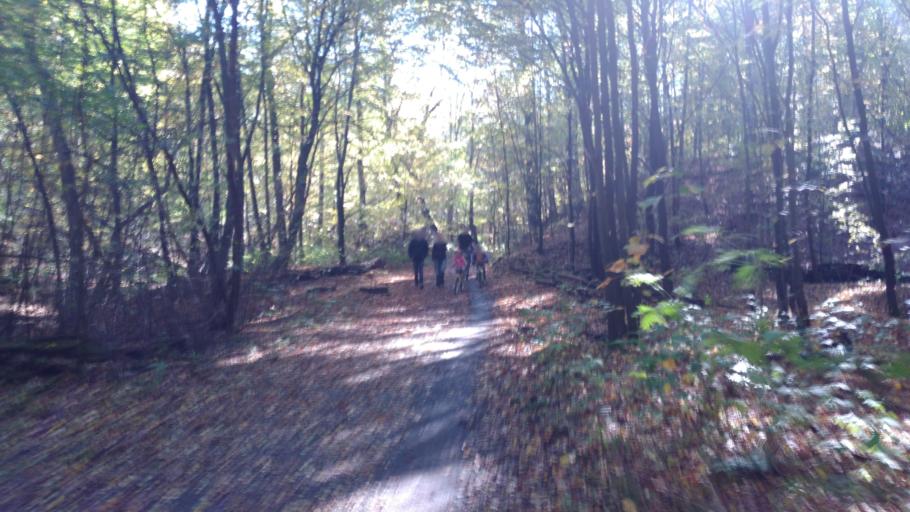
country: DE
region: Saxony
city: Albertstadt
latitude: 51.0913
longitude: 13.7728
